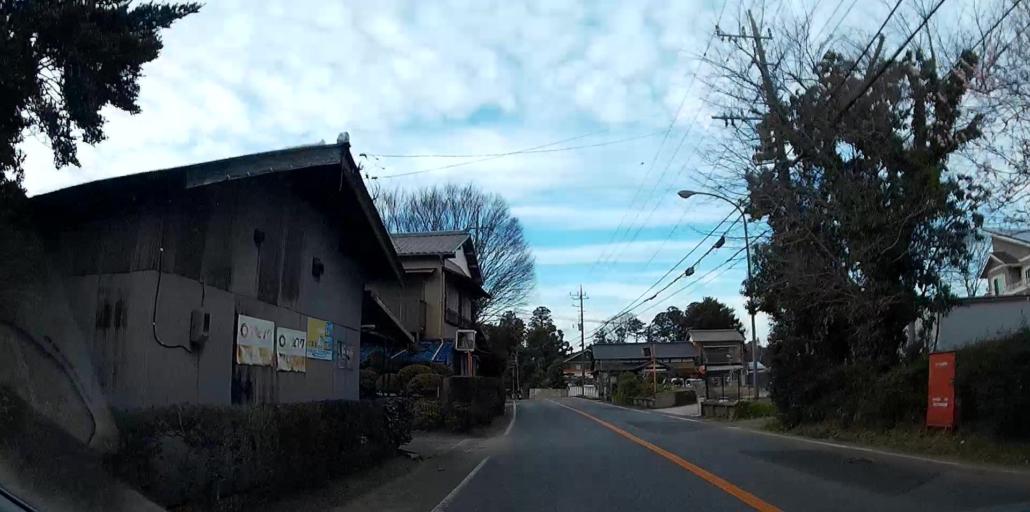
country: JP
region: Chiba
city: Ichihara
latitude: 35.3849
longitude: 140.0637
